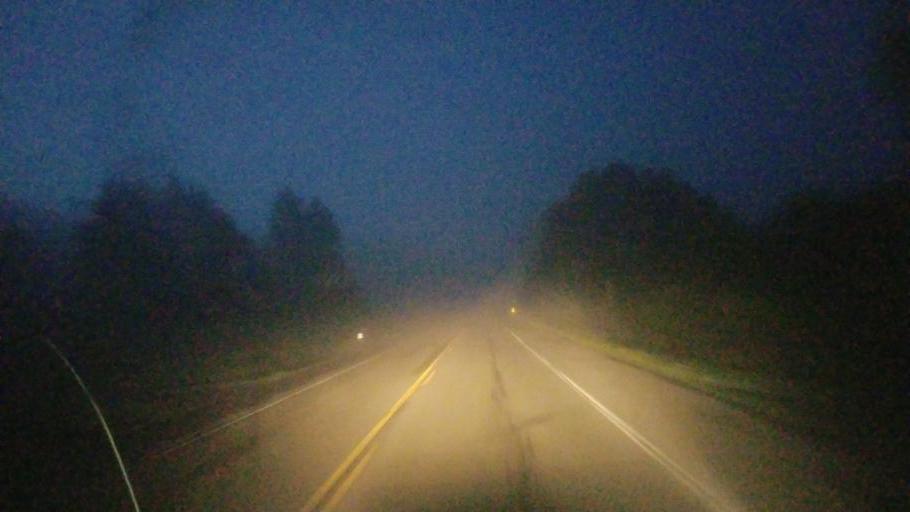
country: US
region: New York
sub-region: Allegany County
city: Wellsville
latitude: 42.0319
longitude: -77.9041
